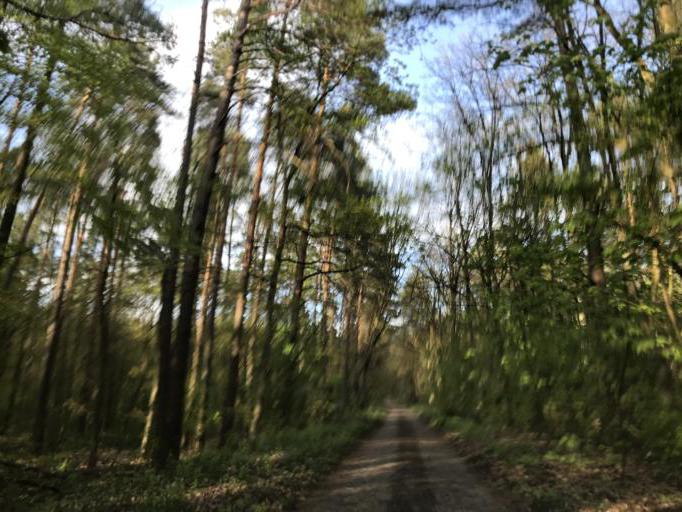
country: DE
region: Brandenburg
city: Joachimsthal
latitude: 52.9672
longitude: 13.7197
